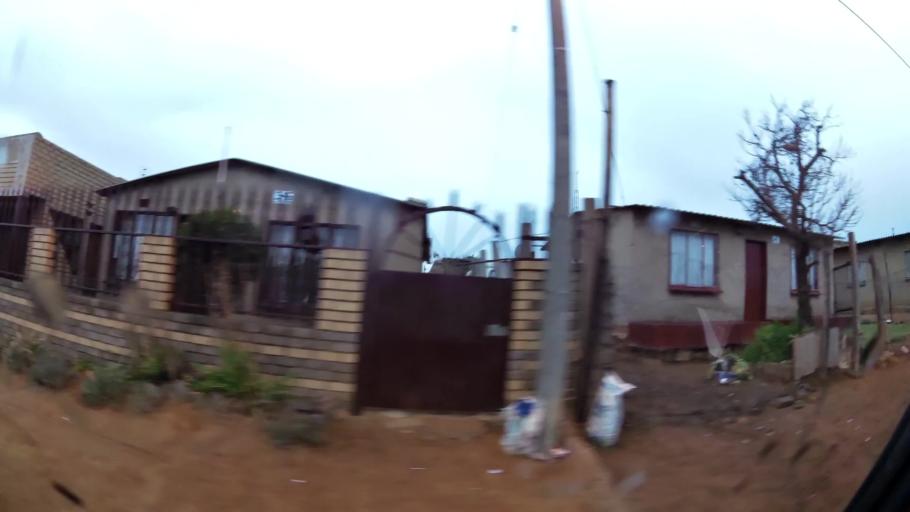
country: ZA
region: Gauteng
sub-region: City of Johannesburg Metropolitan Municipality
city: Roodepoort
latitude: -26.1730
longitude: 27.7912
